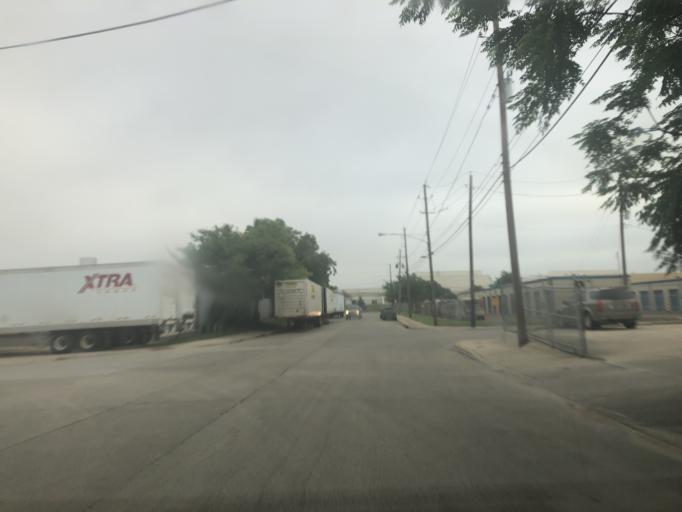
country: US
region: Texas
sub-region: Dallas County
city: Farmers Branch
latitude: 32.8703
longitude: -96.8768
